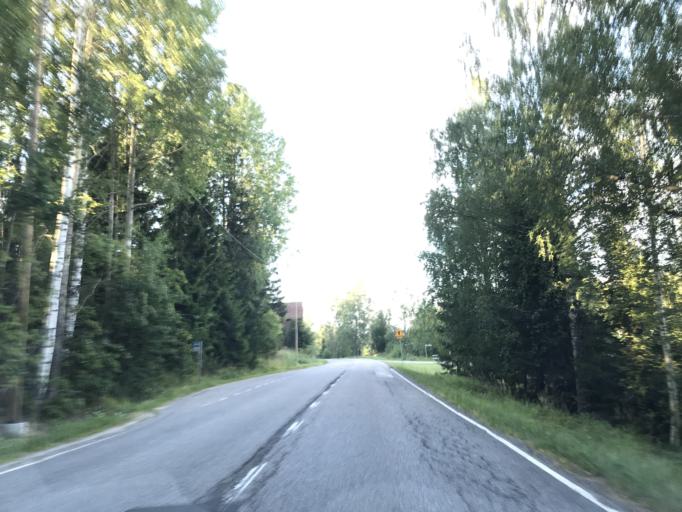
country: FI
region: Uusimaa
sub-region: Helsinki
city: Nurmijaervi
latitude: 60.3728
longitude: 24.6782
